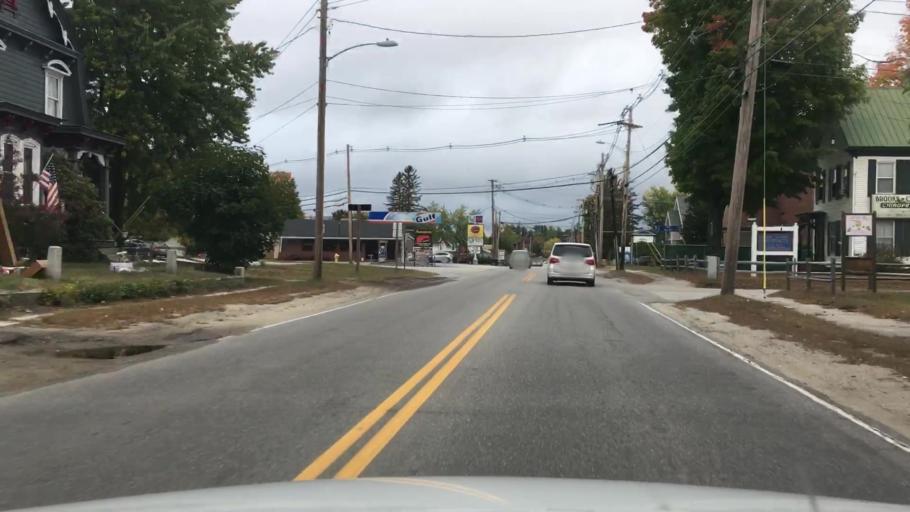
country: US
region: Maine
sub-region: Oxford County
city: Norway
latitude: 44.2084
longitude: -70.5309
